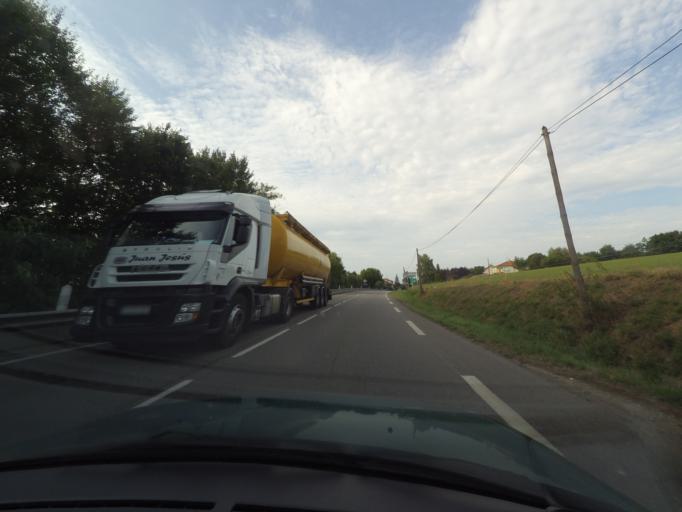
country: FR
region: Limousin
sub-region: Departement de la Haute-Vienne
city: Aixe-sur-Vienne
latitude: 45.7919
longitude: 1.1133
